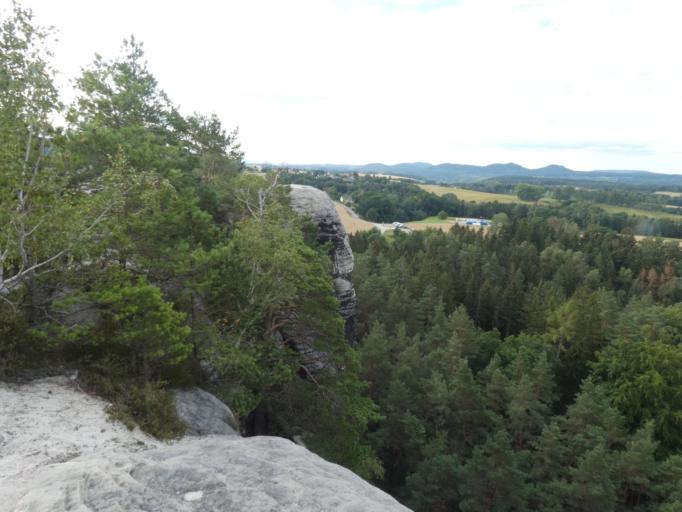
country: DE
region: Saxony
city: Hohnstein
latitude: 50.9583
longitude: 14.0966
